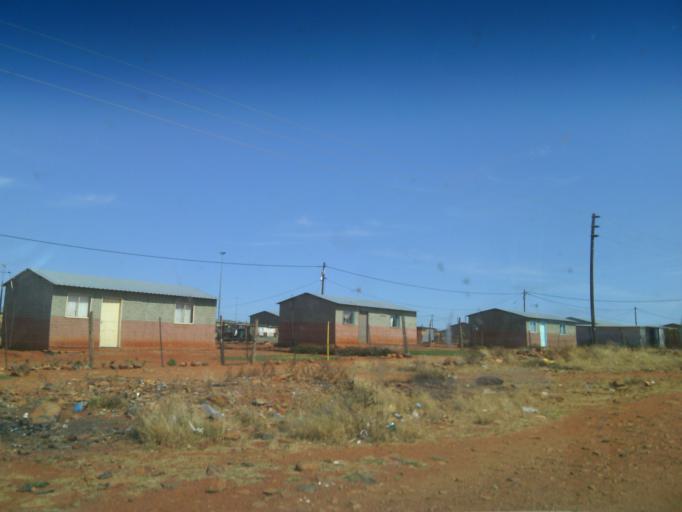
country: ZA
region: Northern Cape
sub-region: Frances Baard District Municipality
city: Barkly West
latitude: -28.5195
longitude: 24.5007
